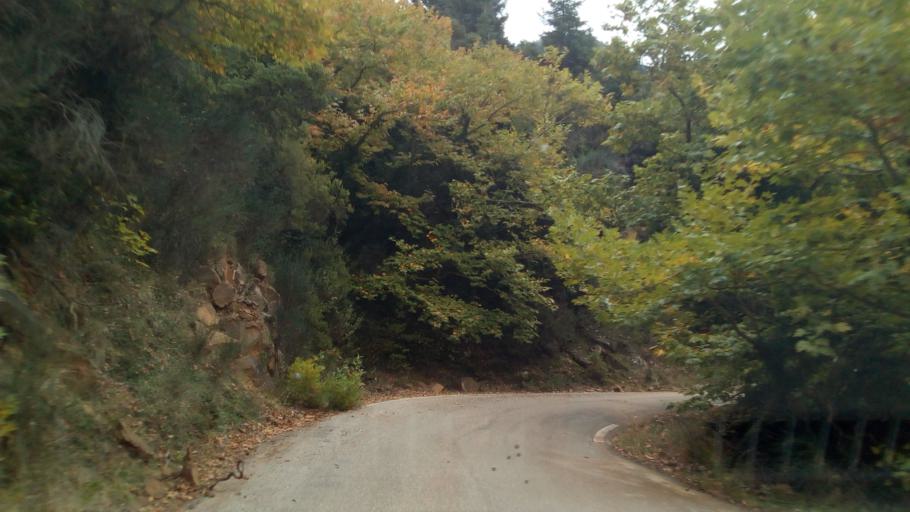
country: GR
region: West Greece
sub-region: Nomos Aitolias kai Akarnanias
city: Thermo
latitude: 38.5857
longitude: 21.8496
